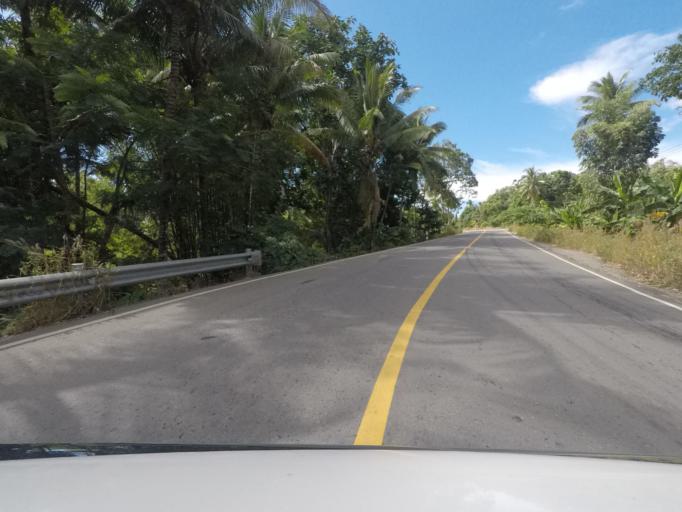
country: TL
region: Baucau
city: Baucau
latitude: -8.4900
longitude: 126.3551
